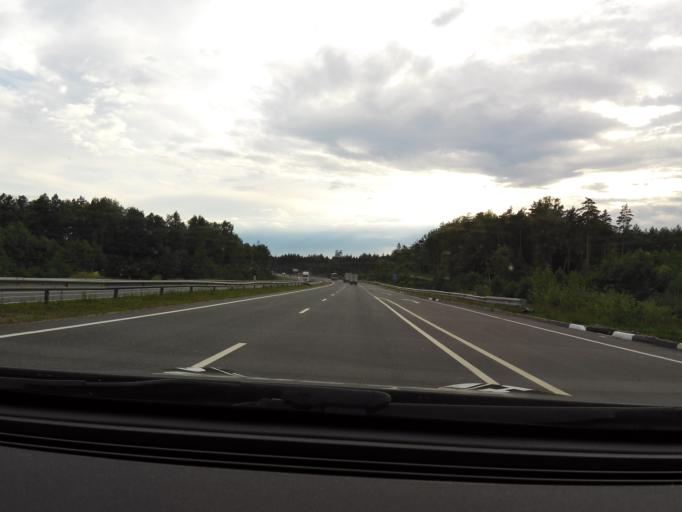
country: RU
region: Vladimir
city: Kommunar
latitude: 56.0867
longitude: 40.4895
